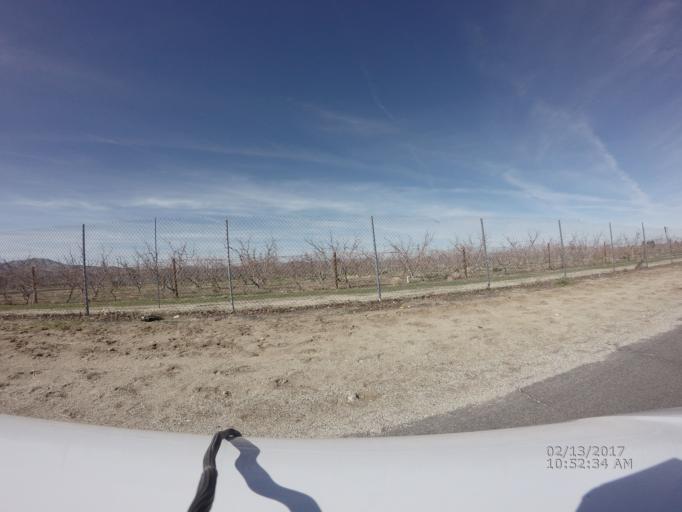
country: US
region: California
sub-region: Los Angeles County
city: Littlerock
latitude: 34.5287
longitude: -117.9794
